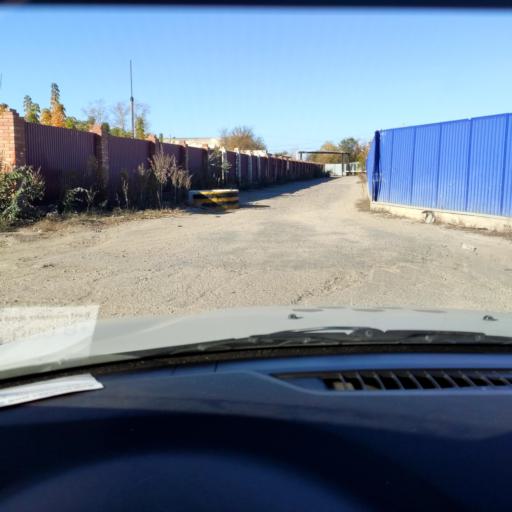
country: RU
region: Samara
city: Tol'yatti
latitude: 53.5309
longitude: 49.4532
